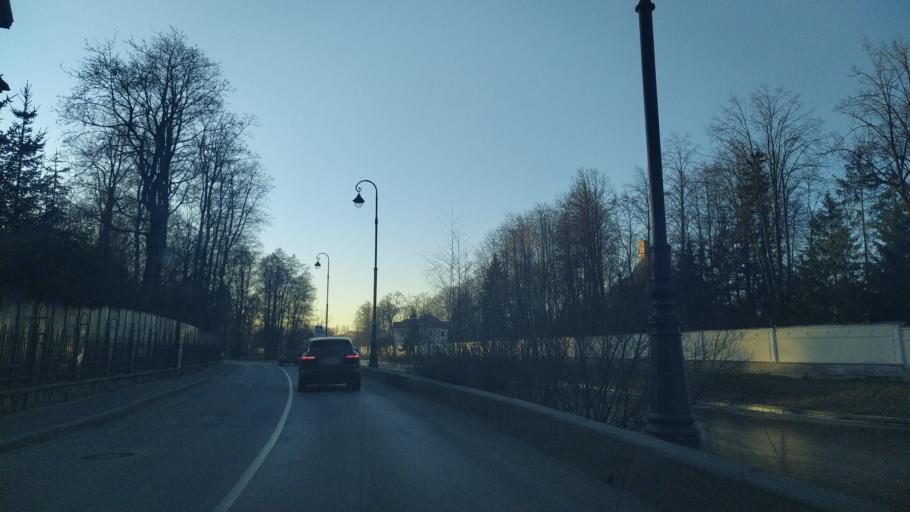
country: RU
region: St.-Petersburg
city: Novaya Derevnya
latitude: 59.9778
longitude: 30.2822
